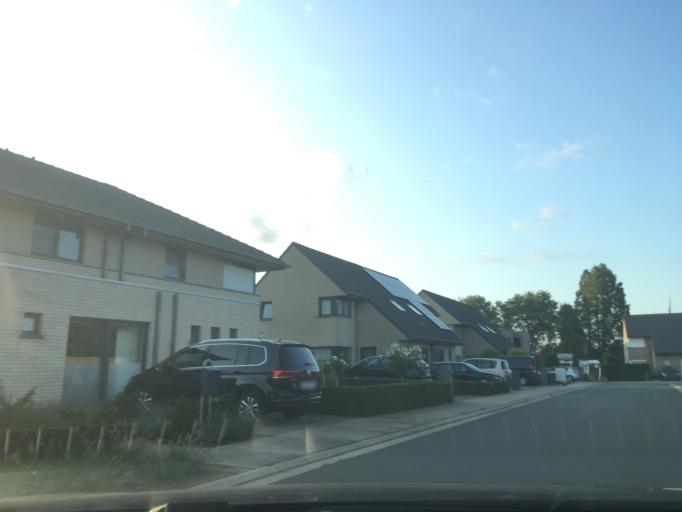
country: BE
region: Flanders
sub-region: Provincie West-Vlaanderen
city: Izegem
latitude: 50.9293
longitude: 3.1686
